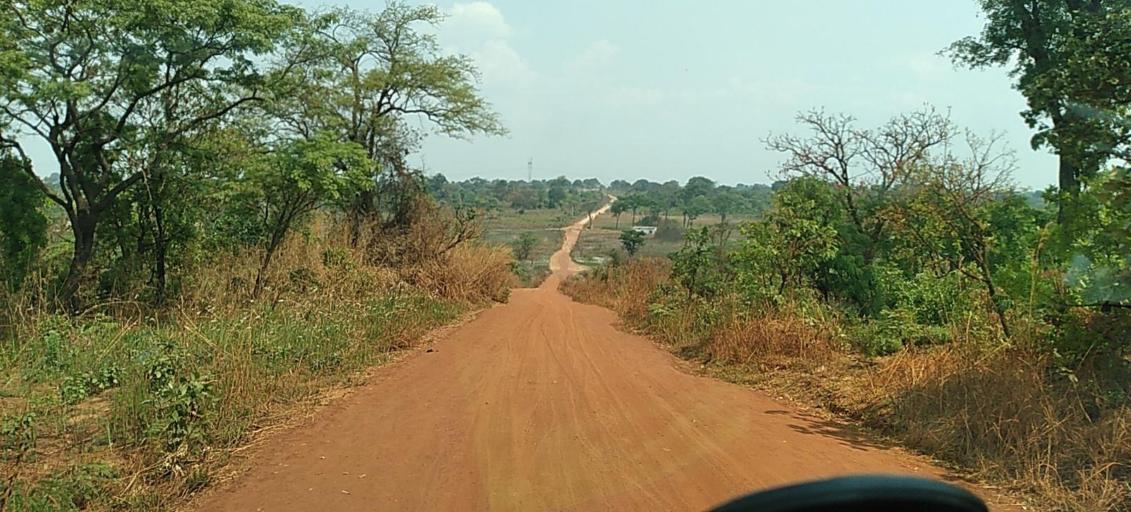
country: ZM
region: North-Western
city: Kansanshi
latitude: -12.1099
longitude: 26.3666
